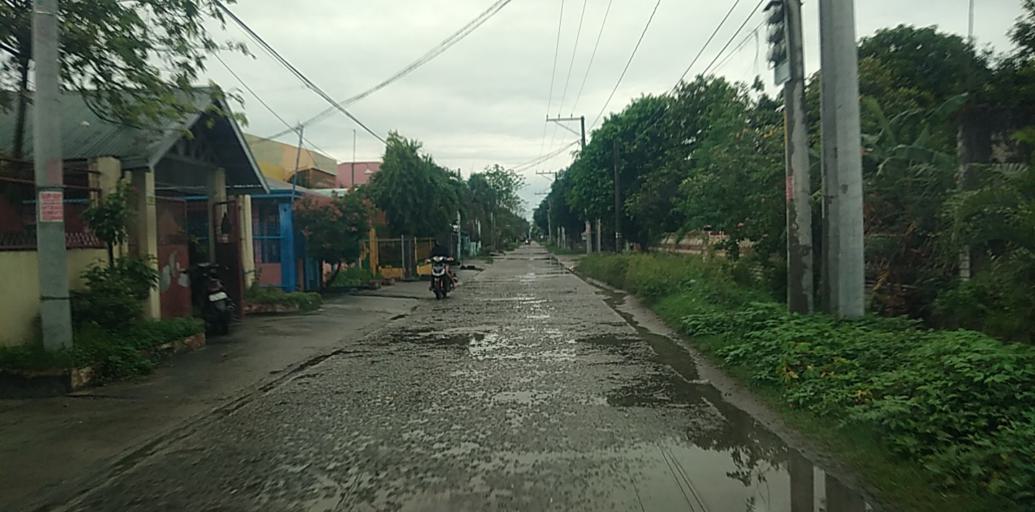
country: PH
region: Central Luzon
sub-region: Province of Pampanga
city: Arayat
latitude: 15.1498
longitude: 120.7417
